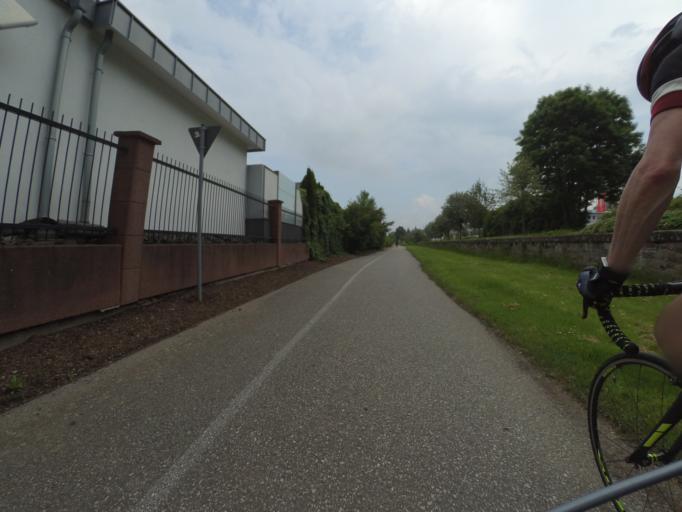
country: DE
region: Rheinland-Pfalz
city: Kastellaun
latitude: 50.0655
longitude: 7.4448
